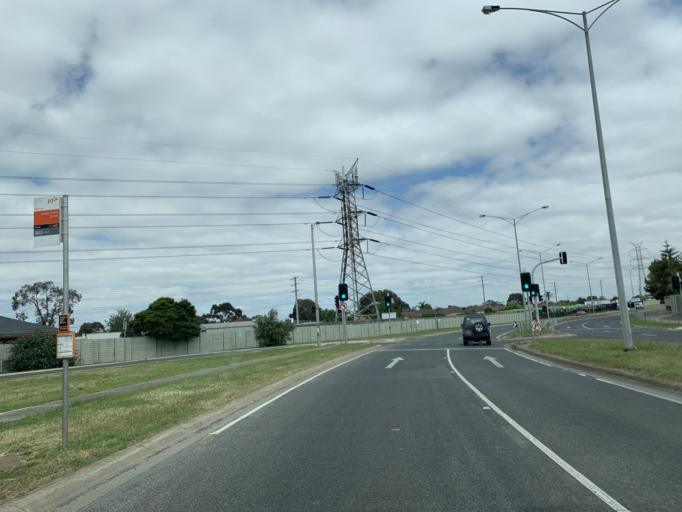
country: AU
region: Victoria
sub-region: Moonee Valley
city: Keilor East
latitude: -37.7405
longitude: 144.8612
